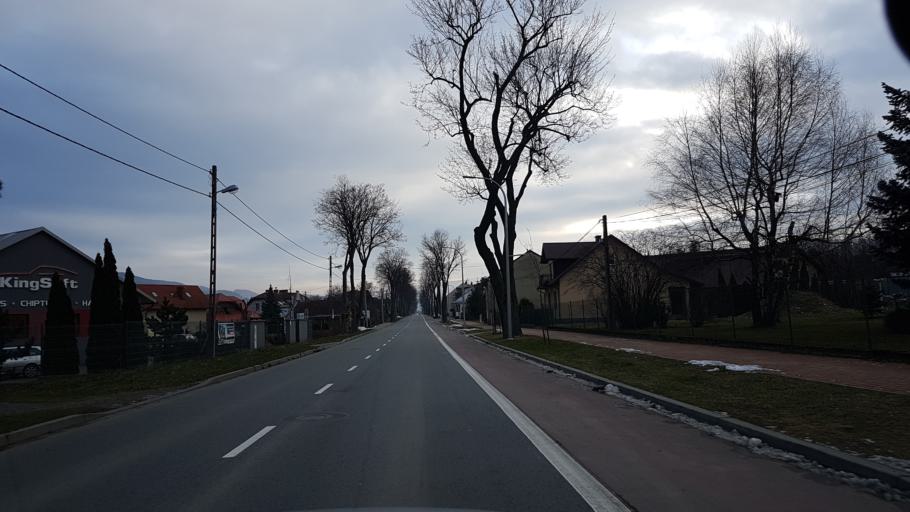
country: PL
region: Lesser Poland Voivodeship
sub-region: Powiat nowosadecki
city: Stary Sacz
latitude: 49.5514
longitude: 20.6403
